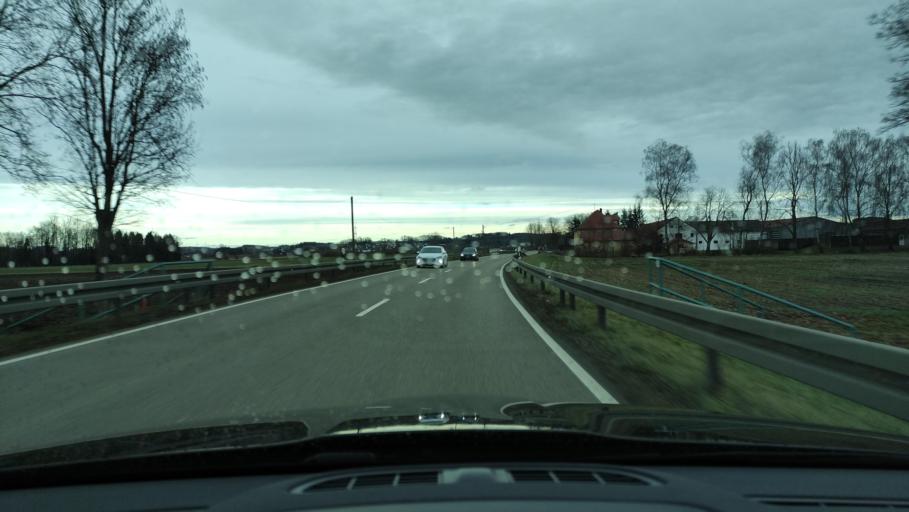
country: DE
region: Bavaria
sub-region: Swabia
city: Buch
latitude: 48.2287
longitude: 10.1430
